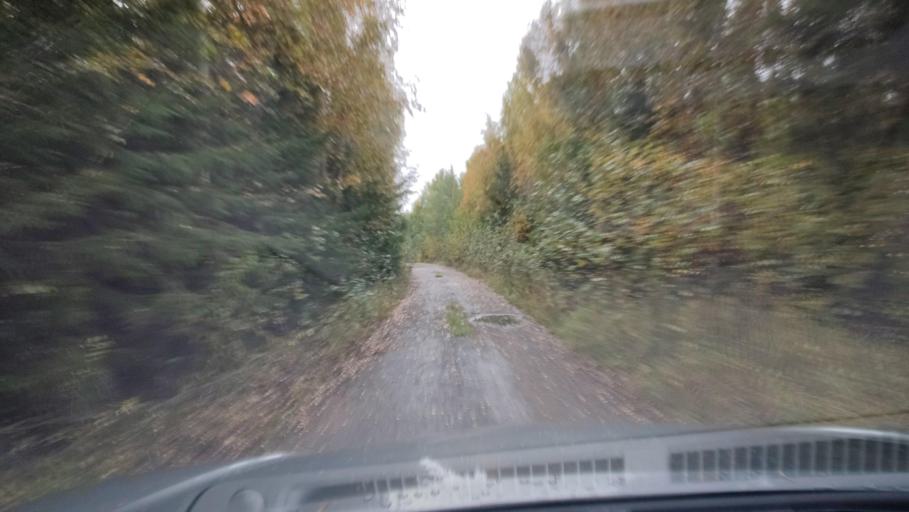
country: FI
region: Ostrobothnia
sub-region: Sydosterbotten
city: Kristinestad
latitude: 62.2688
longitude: 21.4562
